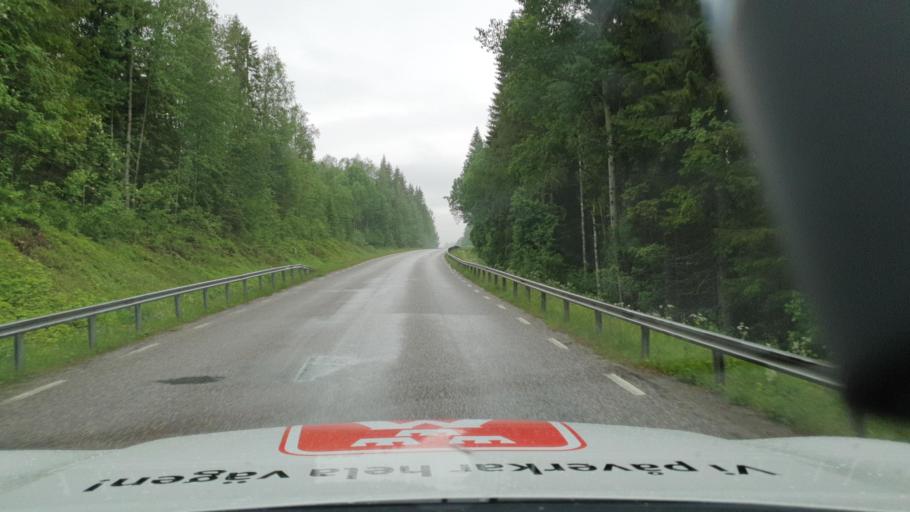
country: SE
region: Vaesterbotten
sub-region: Nordmalings Kommun
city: Nordmaling
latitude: 63.7903
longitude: 19.5547
